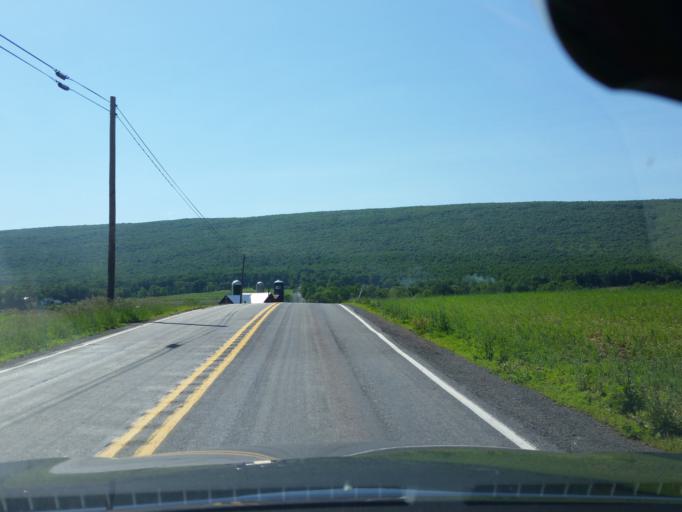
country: US
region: Pennsylvania
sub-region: Lycoming County
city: Duboistown
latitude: 41.1414
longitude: -77.0236
